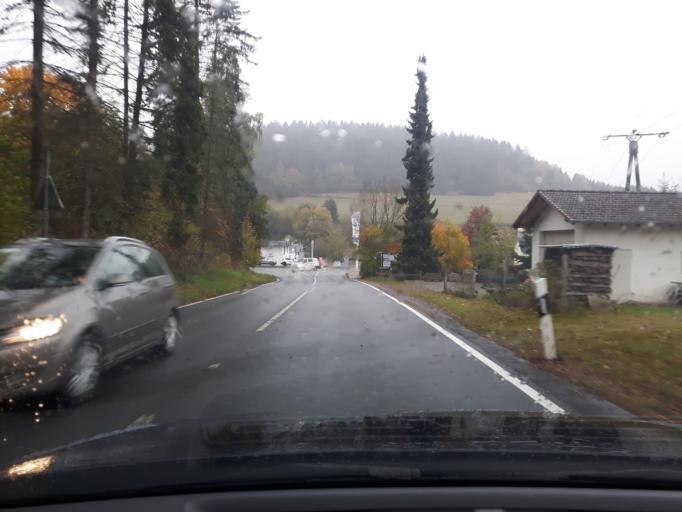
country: DE
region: North Rhine-Westphalia
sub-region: Regierungsbezirk Arnsberg
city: Bad Berleburg
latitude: 51.0136
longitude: 8.4084
